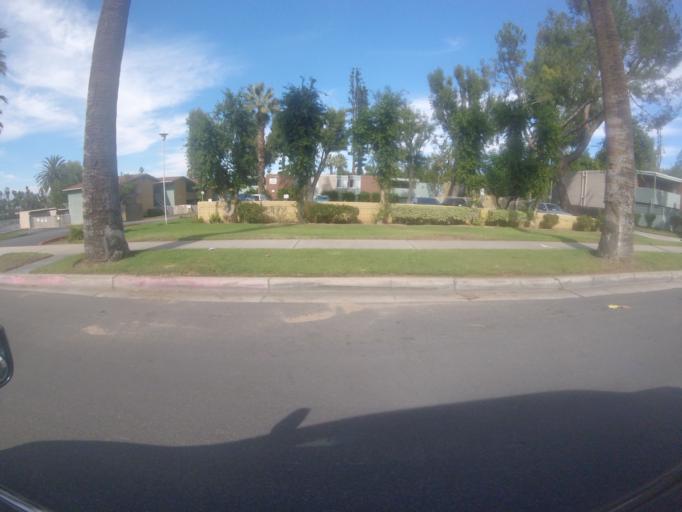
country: US
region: California
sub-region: San Bernardino County
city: Redlands
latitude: 34.0556
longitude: -117.1584
